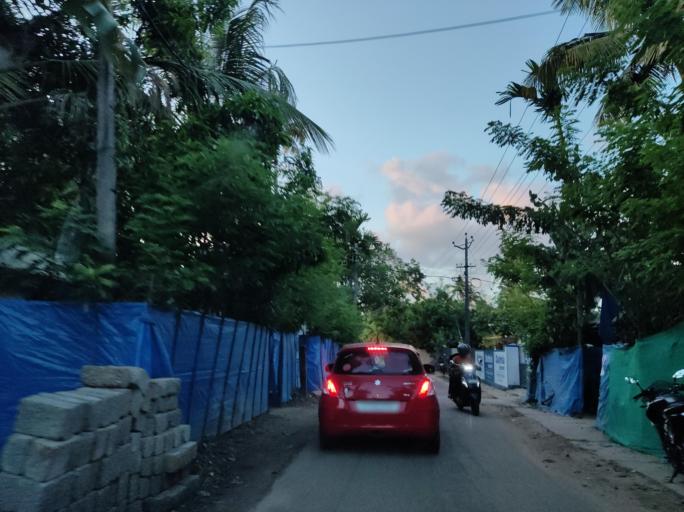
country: IN
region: Kerala
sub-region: Alappuzha
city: Vayalar
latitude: 9.7422
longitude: 76.2876
